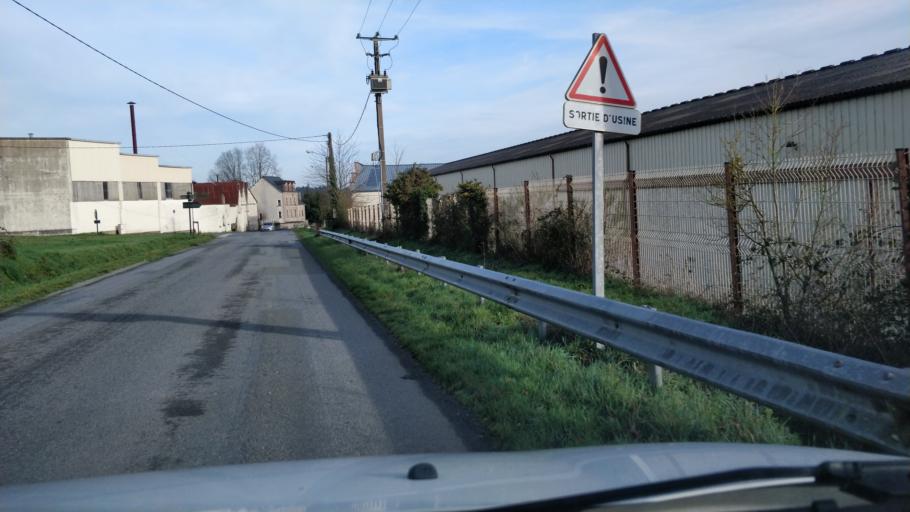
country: FR
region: Brittany
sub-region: Departement d'Ille-et-Vilaine
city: Argentre-du-Plessis
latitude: 48.0510
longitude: -1.1618
